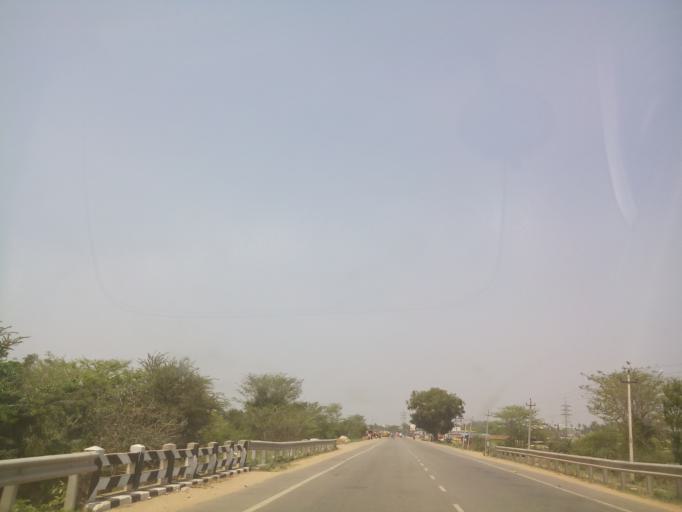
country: IN
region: Karnataka
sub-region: Hassan
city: Hassan
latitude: 12.9905
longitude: 76.0917
